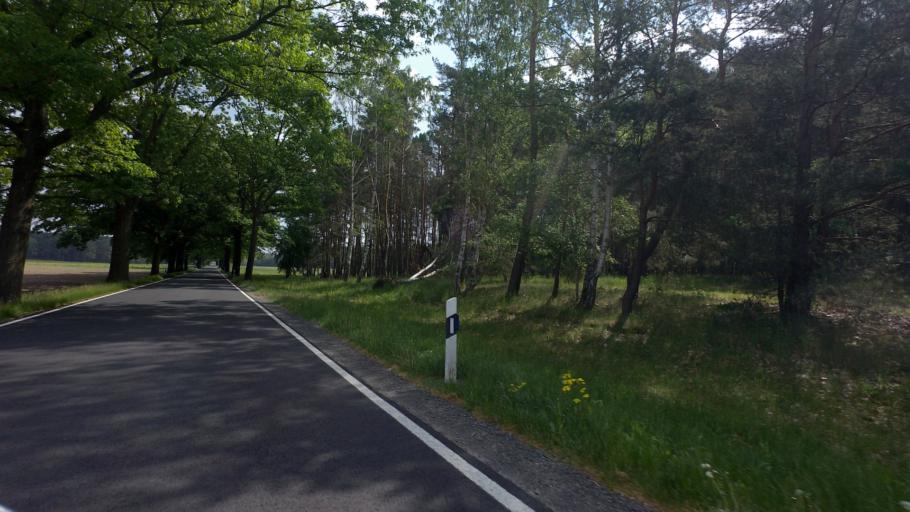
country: DE
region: Brandenburg
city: Neu Zauche
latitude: 51.9991
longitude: 14.1343
